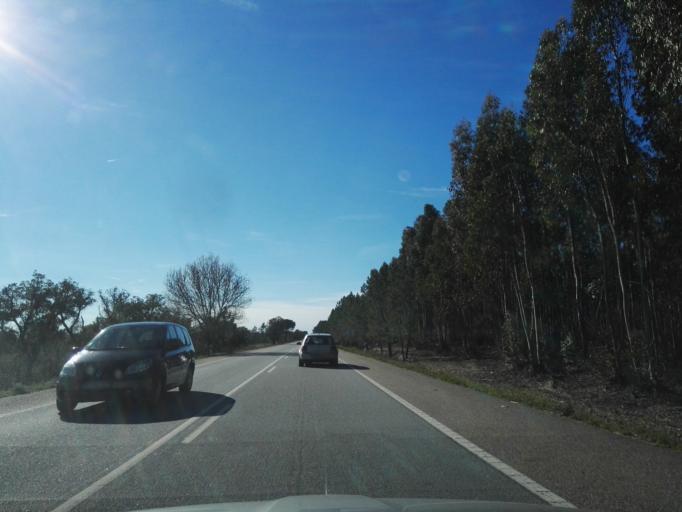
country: PT
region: Portalegre
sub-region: Gaviao
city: Gaviao
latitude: 39.4464
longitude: -7.8159
